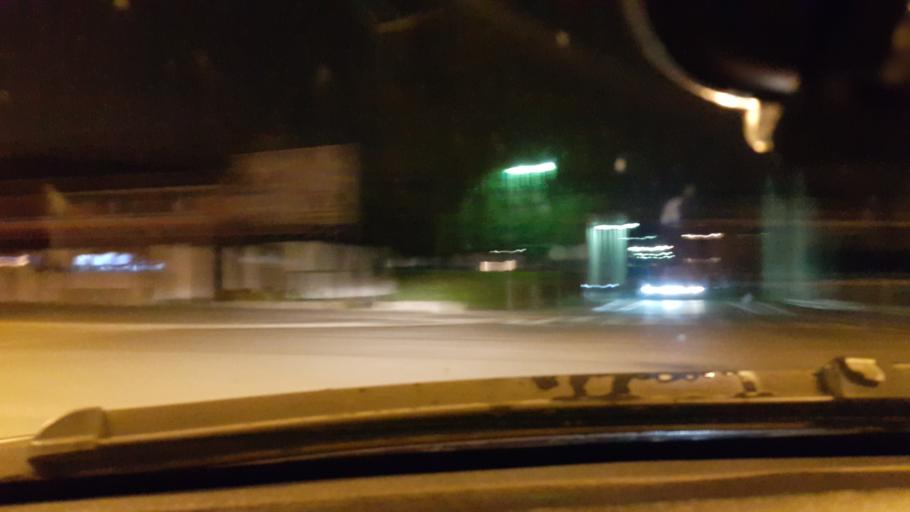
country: SI
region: Maribor
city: Maribor
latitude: 46.5347
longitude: 15.6647
